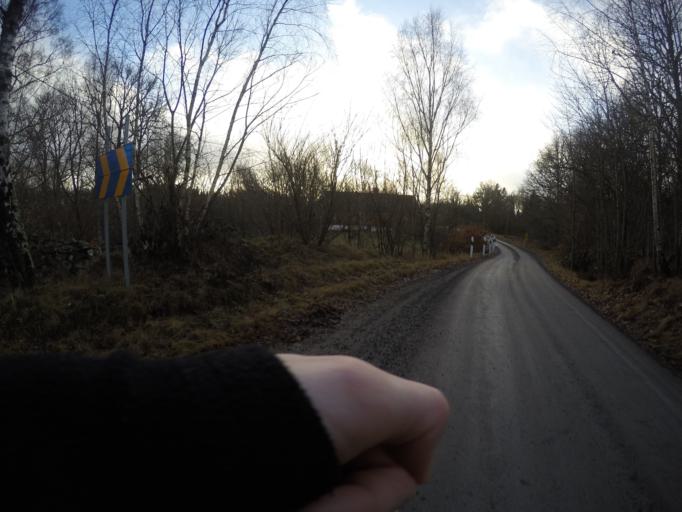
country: SE
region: Skane
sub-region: Osby Kommun
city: Lonsboda
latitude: 56.3772
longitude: 14.3381
